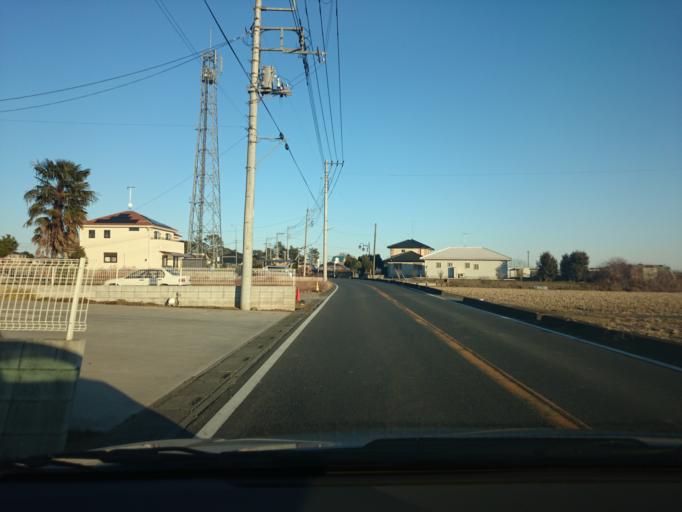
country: JP
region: Saitama
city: Kisai
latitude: 36.1116
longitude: 139.5790
